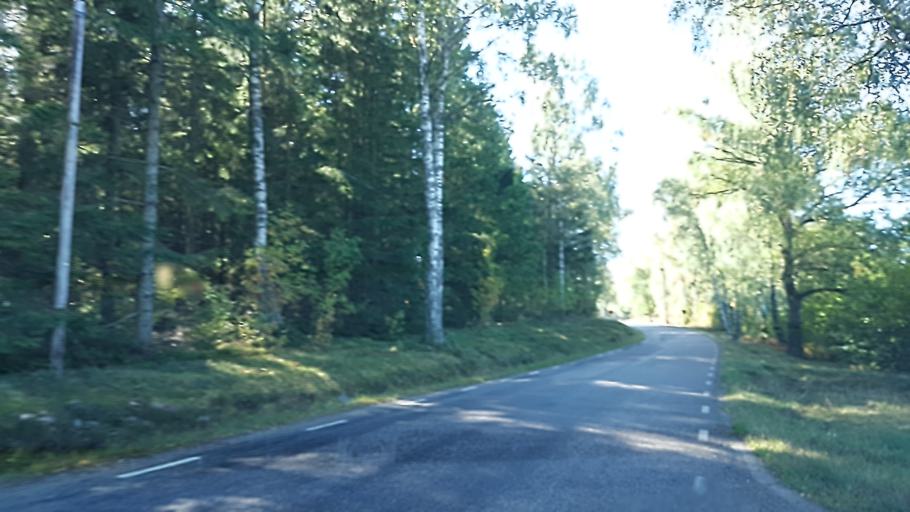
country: SE
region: Kronoberg
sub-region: Ljungby Kommun
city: Ljungby
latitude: 56.8035
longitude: 14.0339
